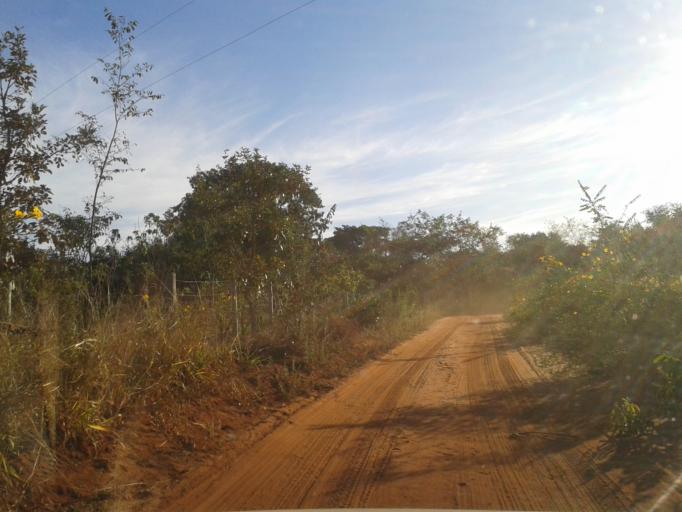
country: BR
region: Minas Gerais
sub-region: Santa Vitoria
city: Santa Vitoria
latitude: -18.9979
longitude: -50.3786
